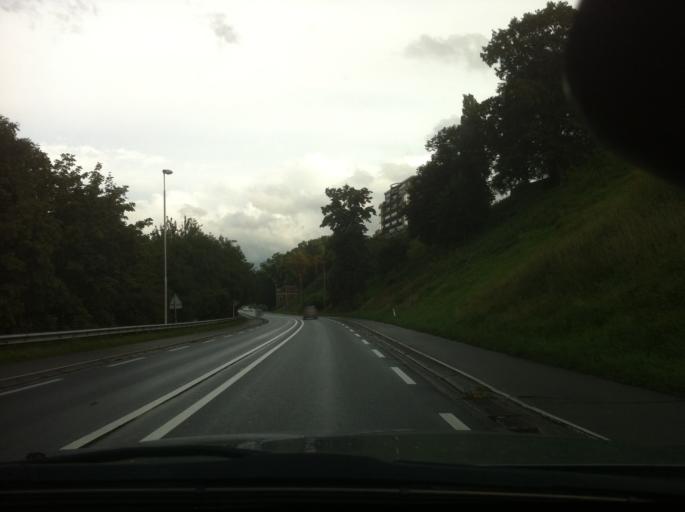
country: NL
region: Gelderland
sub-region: Gemeente Nijmegen
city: Nijmegen
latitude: 51.8454
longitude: 5.8782
